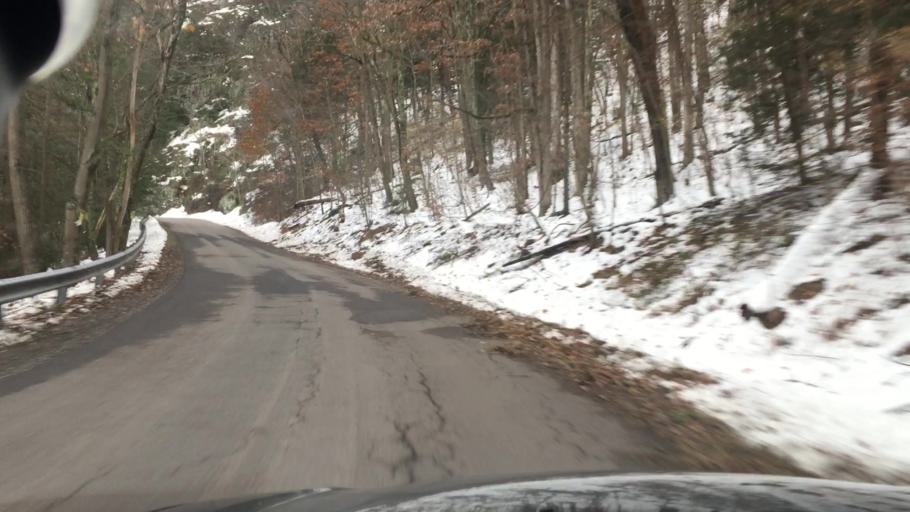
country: US
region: Pennsylvania
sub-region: Luzerne County
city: Conyngham
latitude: 41.0121
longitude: -76.1013
